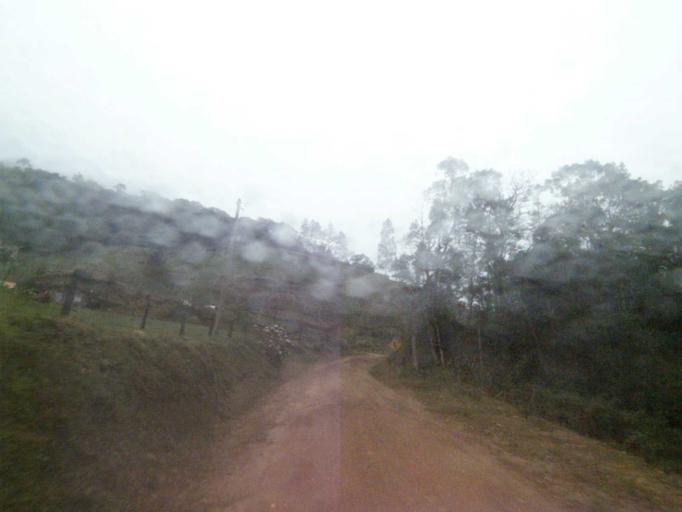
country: BR
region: Santa Catarina
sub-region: Anitapolis
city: Anitapolis
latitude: -27.8754
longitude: -49.1332
